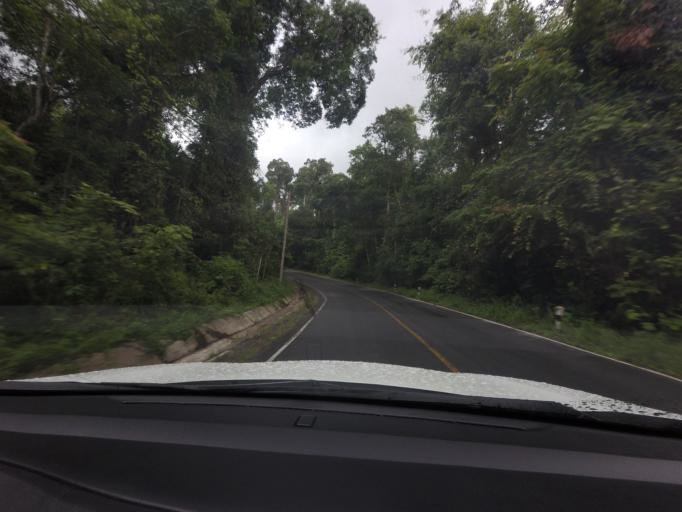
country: TH
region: Nakhon Ratchasima
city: Pak Chong
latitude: 14.4651
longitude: 101.3725
